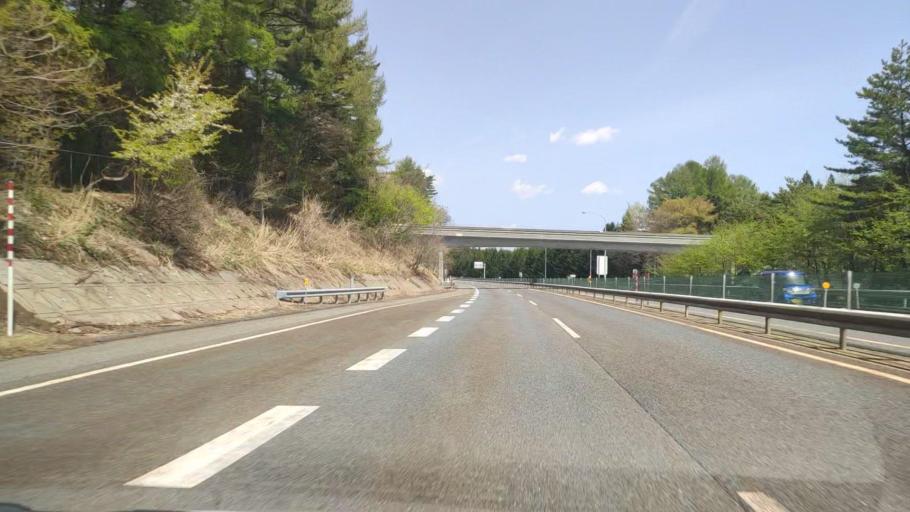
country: JP
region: Iwate
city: Ichinohe
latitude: 40.2537
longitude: 141.4027
